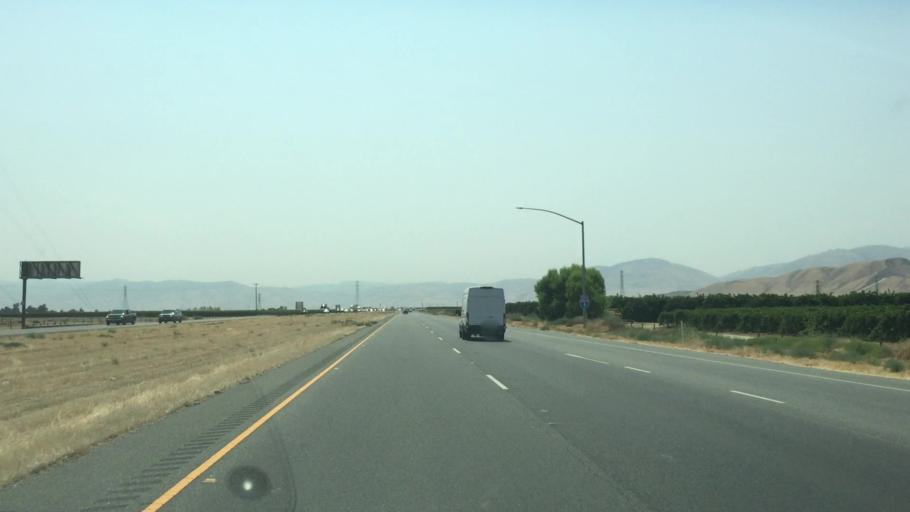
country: US
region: California
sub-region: Kern County
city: Weedpatch
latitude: 35.0567
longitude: -118.9966
